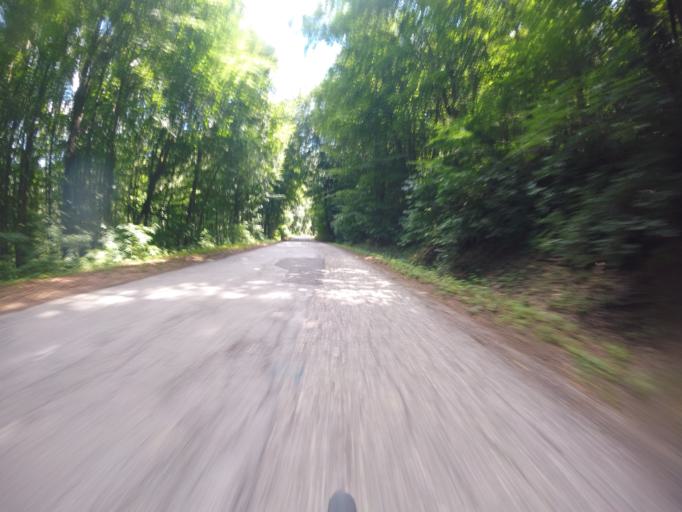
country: HR
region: Karlovacka
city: Ozalj
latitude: 45.6721
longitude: 15.4664
